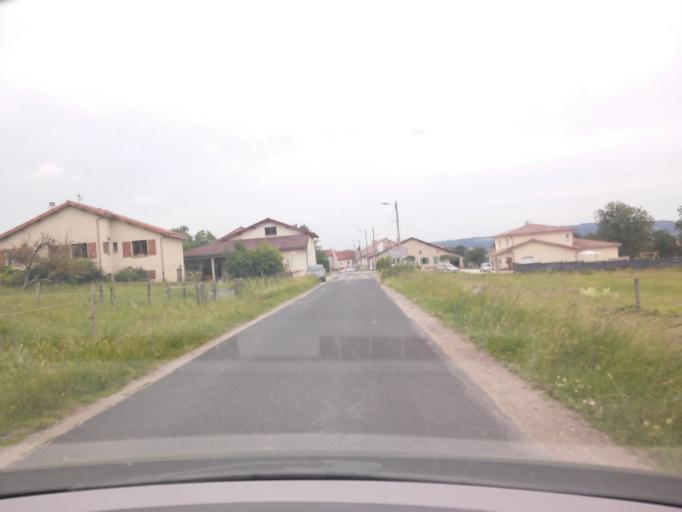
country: FR
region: Lorraine
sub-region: Departement de la Meuse
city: Vignot
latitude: 48.8001
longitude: 5.6581
